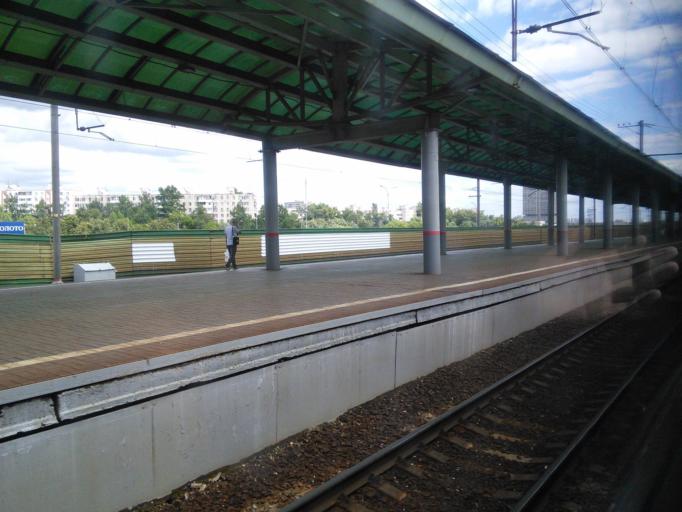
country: RU
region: Moscow
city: Veshnyaki
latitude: 55.7157
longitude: 37.8185
